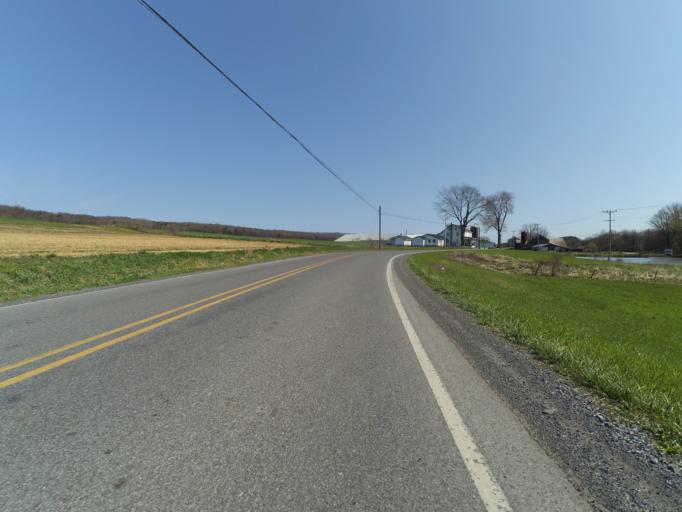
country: US
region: Pennsylvania
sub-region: Centre County
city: Zion
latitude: 40.9704
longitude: -77.6015
